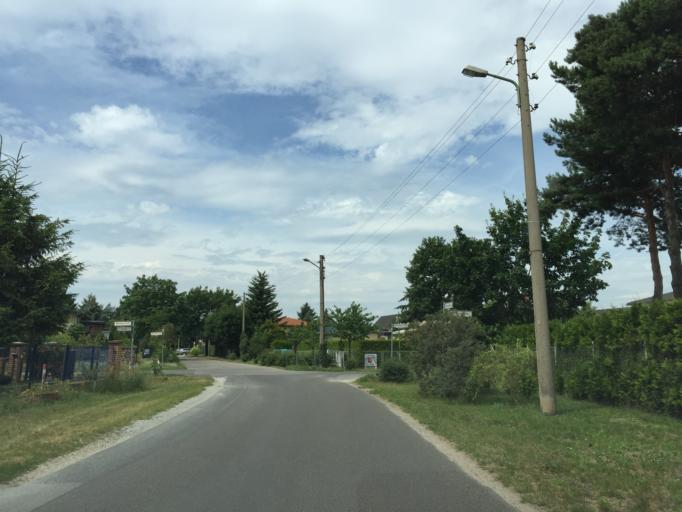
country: DE
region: Berlin
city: Mahlsdorf
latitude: 52.4912
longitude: 13.6128
